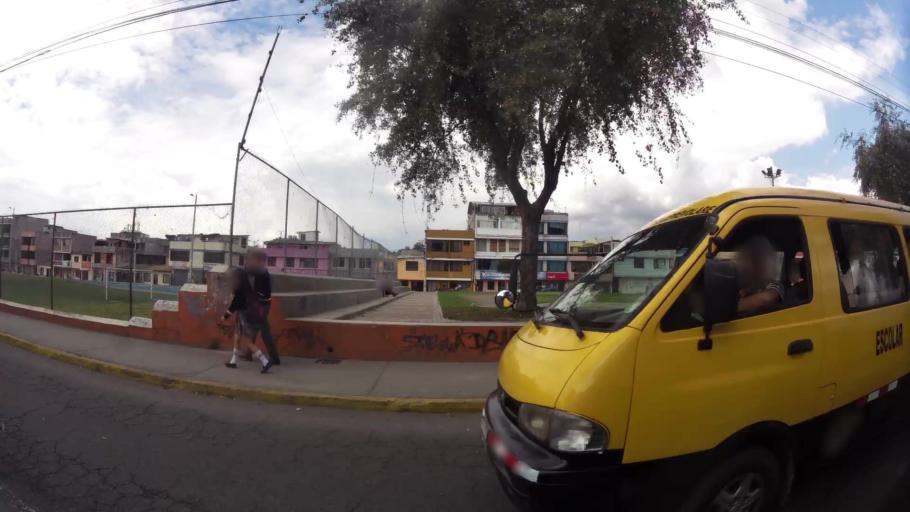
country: EC
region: Pichincha
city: Quito
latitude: -0.0985
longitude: -78.4531
